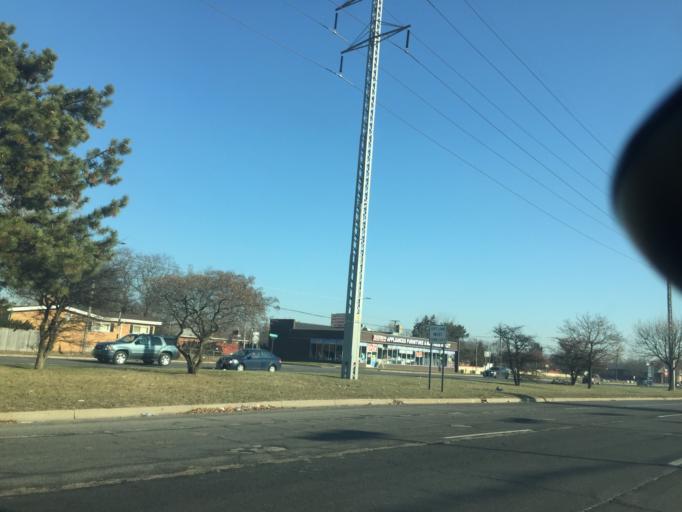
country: US
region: Michigan
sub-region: Macomb County
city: Eastpointe
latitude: 42.4501
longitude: -82.9561
